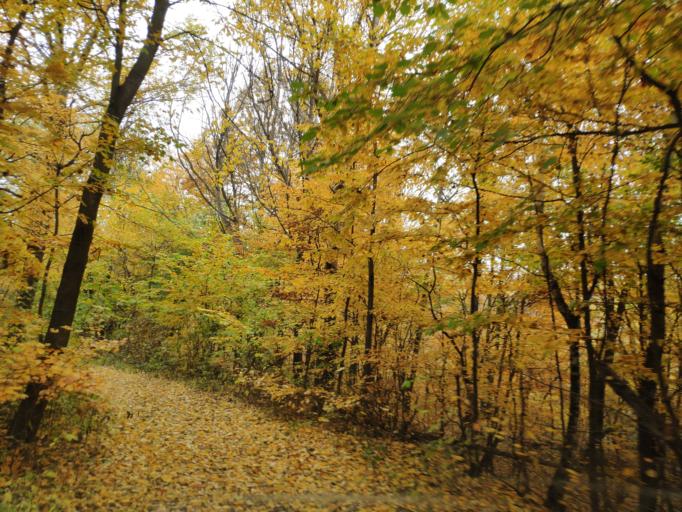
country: SK
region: Kosicky
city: Kosice
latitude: 48.7251
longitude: 21.1100
